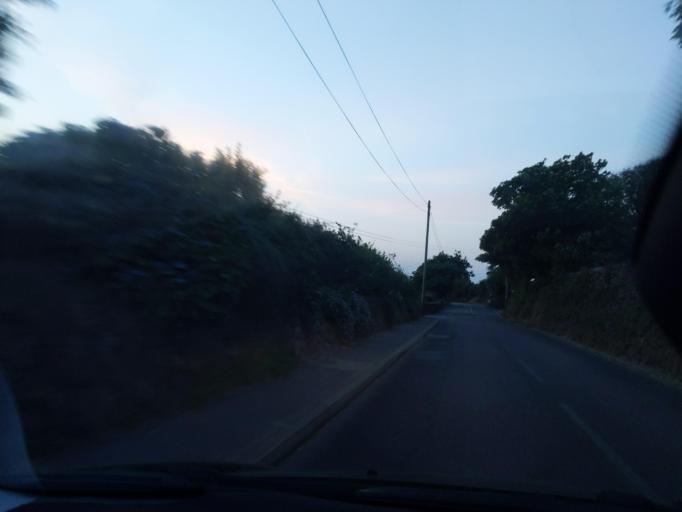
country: GB
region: England
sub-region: Cornwall
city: Camborne
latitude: 50.1785
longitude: -5.3117
